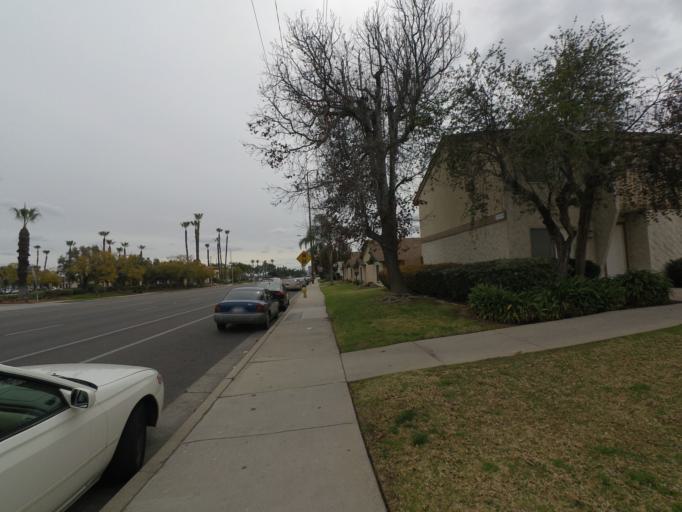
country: US
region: California
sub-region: Riverside County
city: March Air Force Base
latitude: 33.9190
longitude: -117.2613
